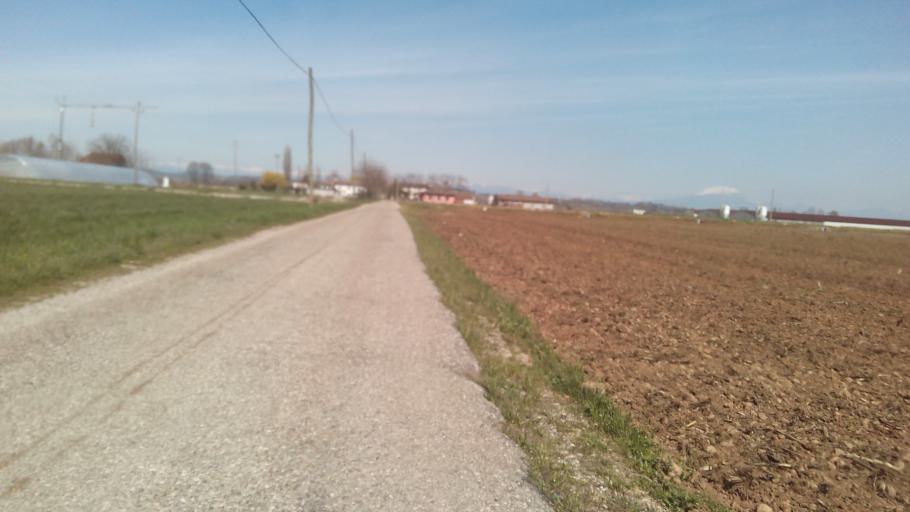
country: IT
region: Lombardy
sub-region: Provincia di Mantova
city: Cerlongo
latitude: 45.2794
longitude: 10.6697
